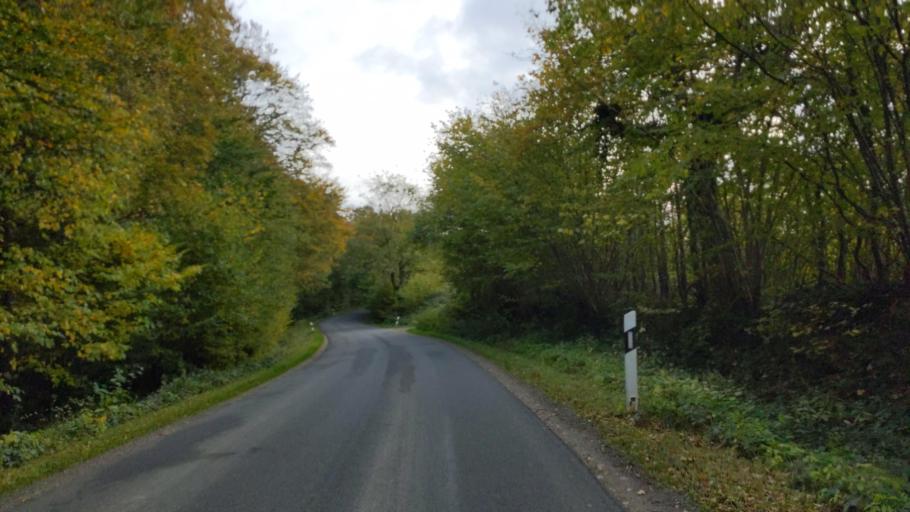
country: DE
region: Schleswig-Holstein
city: Susel
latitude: 54.0556
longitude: 10.7219
